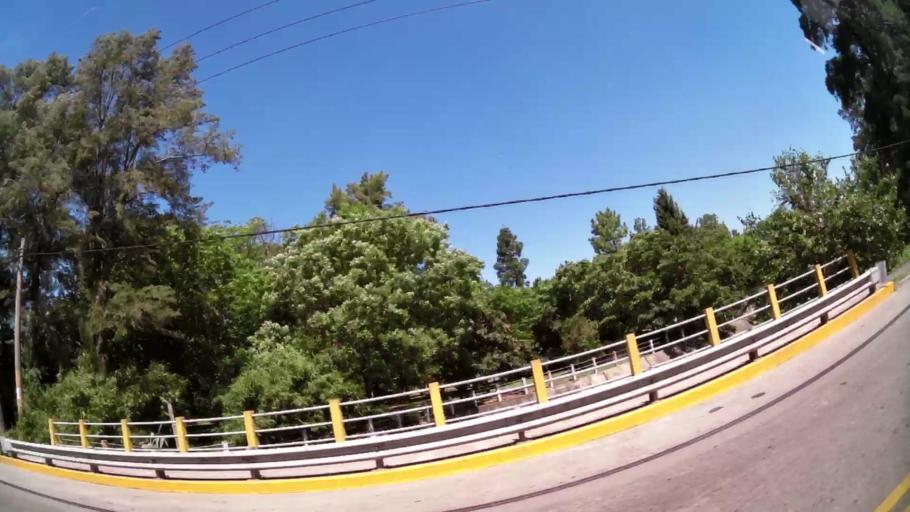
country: AR
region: Buenos Aires
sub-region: Partido de Tigre
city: Tigre
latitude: -34.4874
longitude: -58.6458
